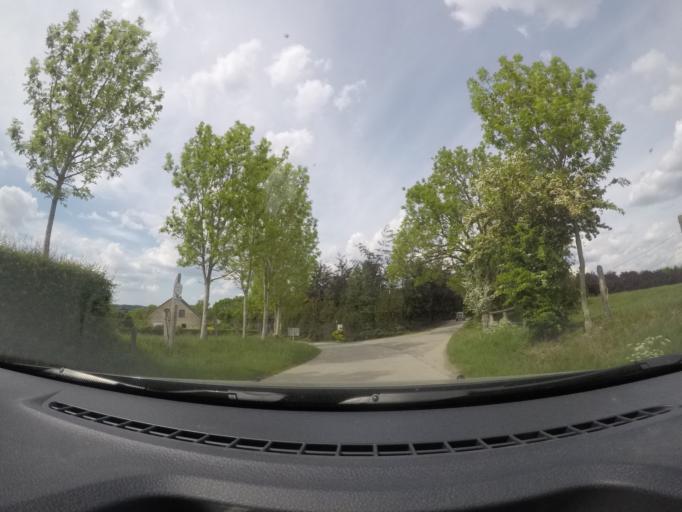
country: BE
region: Wallonia
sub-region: Province du Luxembourg
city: Leglise
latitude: 49.8102
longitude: 5.5606
